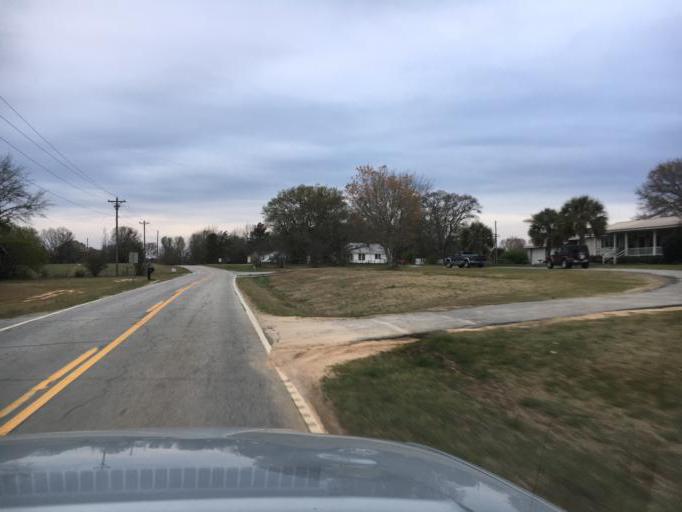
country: US
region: South Carolina
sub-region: Laurens County
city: Laurens
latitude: 34.5445
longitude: -82.0864
